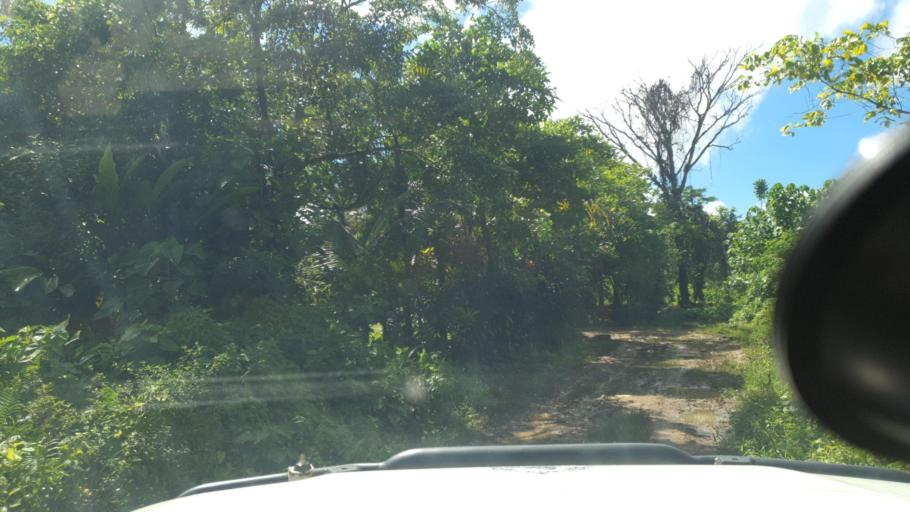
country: SB
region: Western Province
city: Gizo
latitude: -8.2487
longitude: 157.2011
